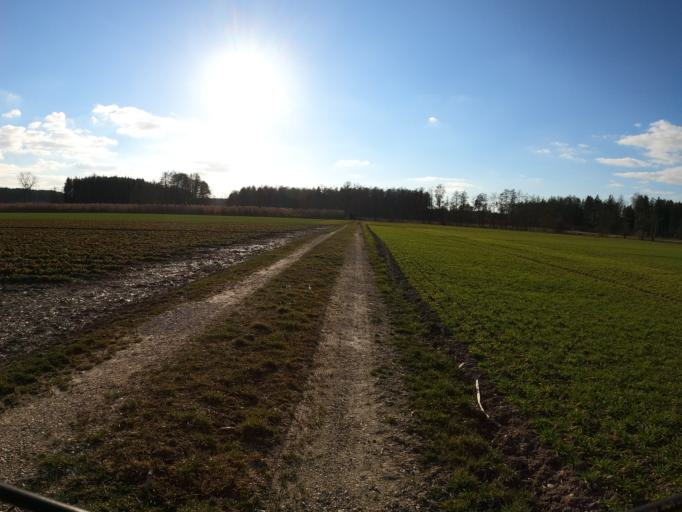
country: DE
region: Bavaria
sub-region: Swabia
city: Bubesheim
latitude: 48.4160
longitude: 10.2280
